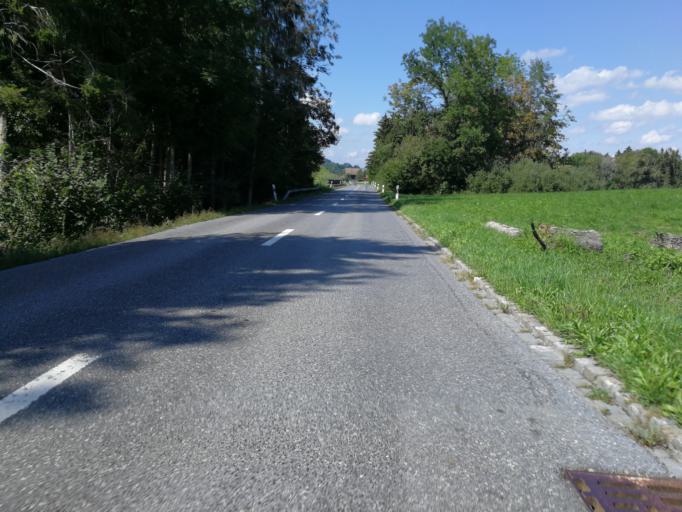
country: CH
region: Zurich
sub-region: Bezirk Horgen
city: Au
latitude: 47.2211
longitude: 8.6320
